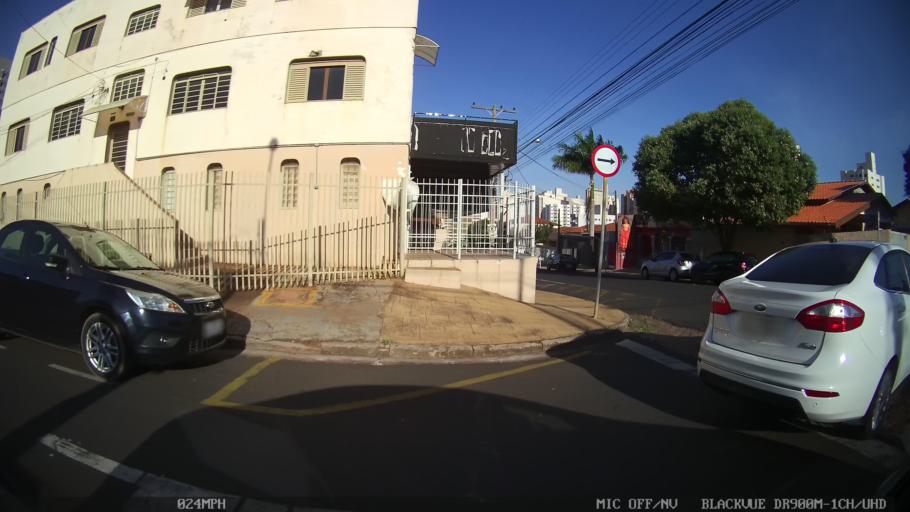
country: BR
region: Sao Paulo
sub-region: Sao Jose Do Rio Preto
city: Sao Jose do Rio Preto
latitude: -20.8096
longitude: -49.3882
